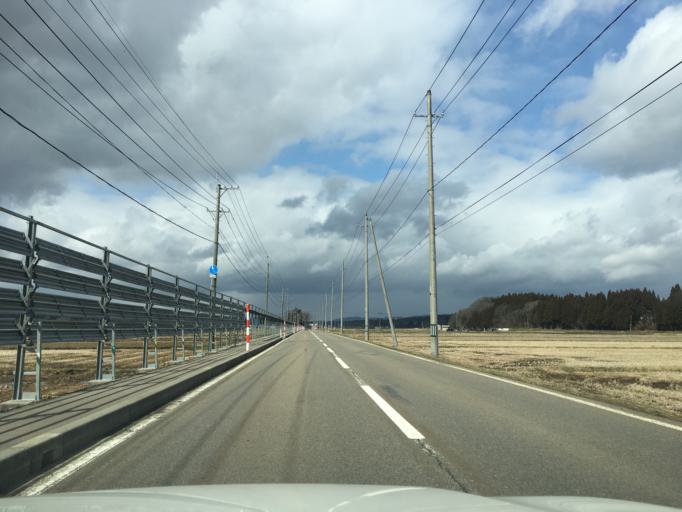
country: JP
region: Akita
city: Takanosu
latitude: 40.1291
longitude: 140.3619
